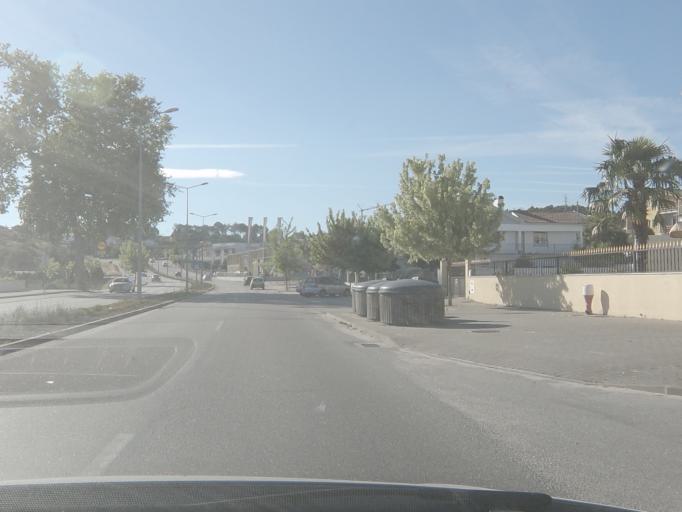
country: PT
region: Viseu
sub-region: Viseu
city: Abraveses
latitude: 40.6915
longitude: -7.9273
